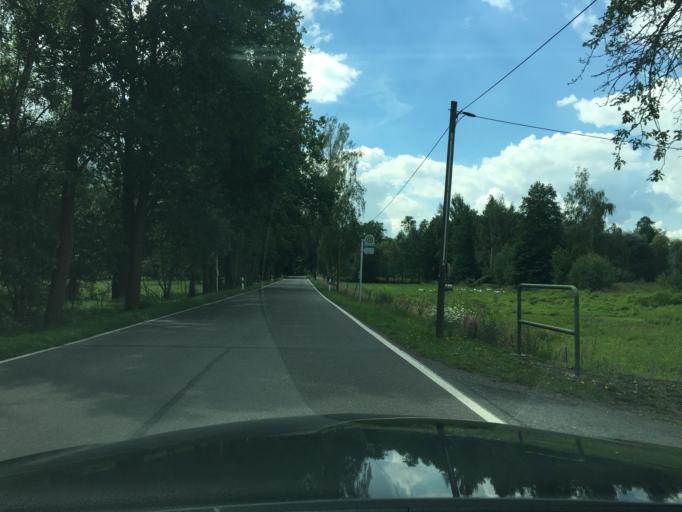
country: DE
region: Brandenburg
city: Burg
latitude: 51.8310
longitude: 14.1045
